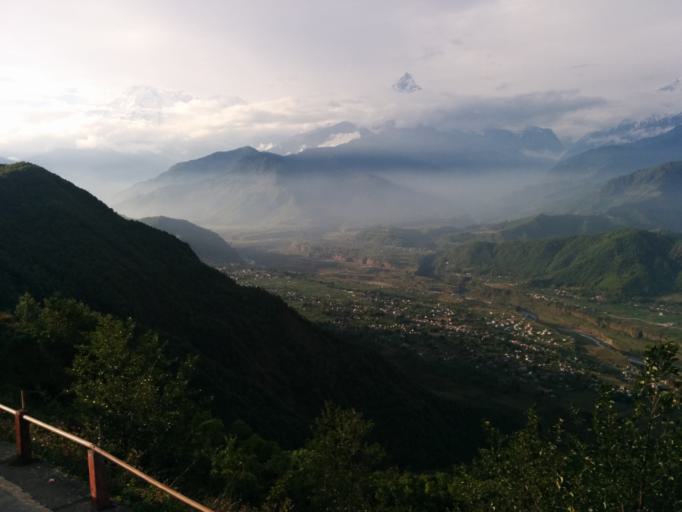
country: NP
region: Western Region
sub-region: Gandaki Zone
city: Pokhara
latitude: 28.2462
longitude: 83.9487
